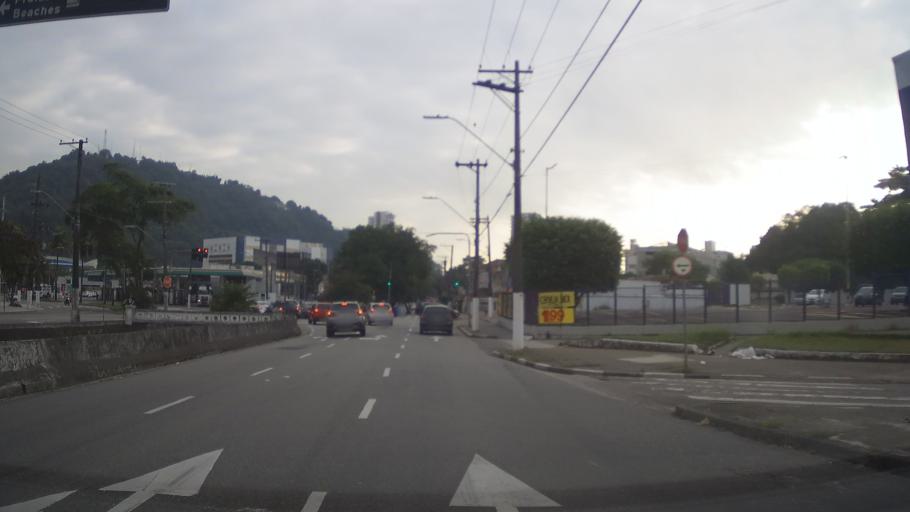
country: BR
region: Sao Paulo
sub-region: Santos
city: Santos
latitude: -23.9473
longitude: -46.3362
